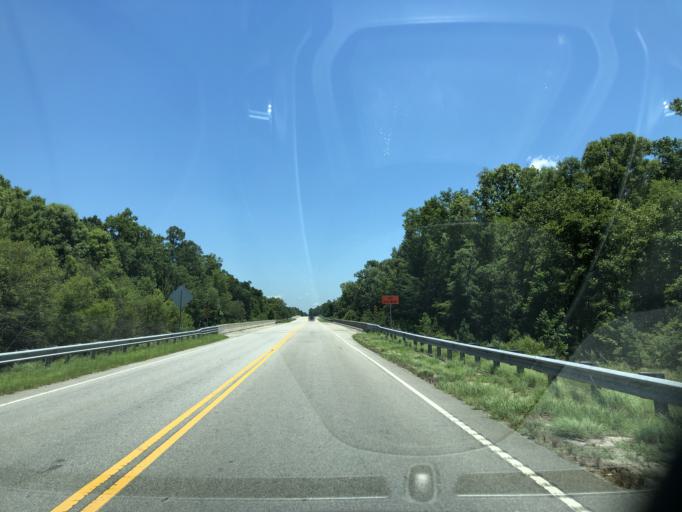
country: US
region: South Carolina
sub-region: Orangeburg County
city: Branchville
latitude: 33.2400
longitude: -80.8601
